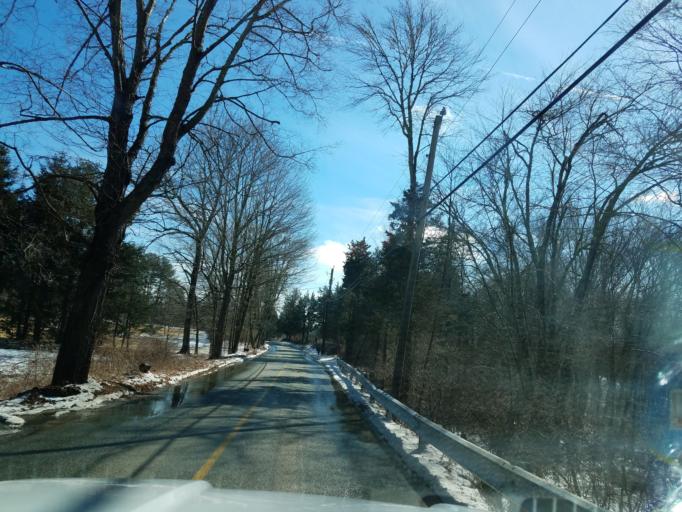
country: US
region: Connecticut
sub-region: New London County
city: Preston City
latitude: 41.5009
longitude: -71.9100
